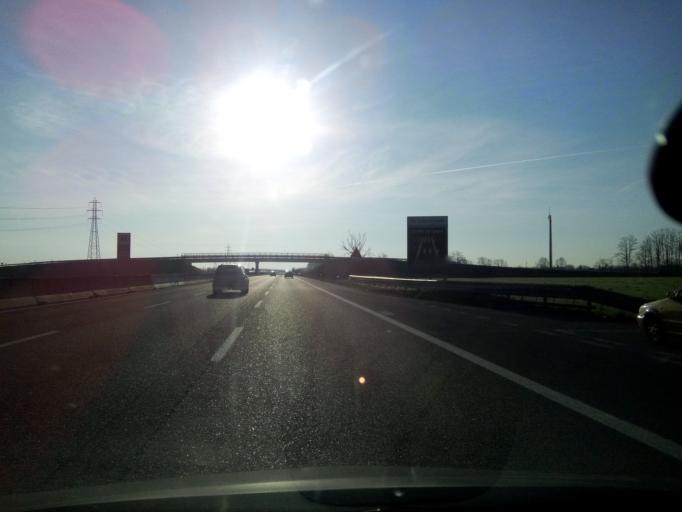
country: IT
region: Emilia-Romagna
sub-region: Provincia di Parma
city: Fidenza
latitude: 44.8877
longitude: 10.0992
